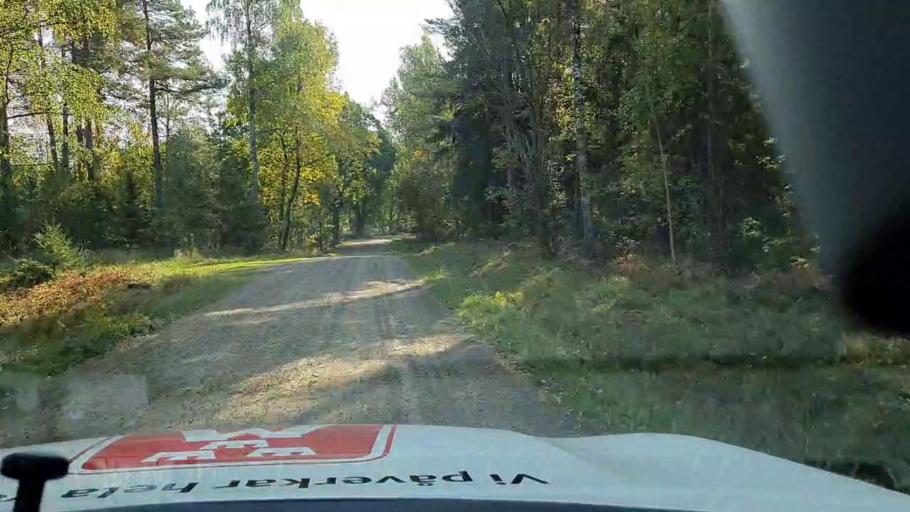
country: SE
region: Soedermanland
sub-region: Eskilstuna Kommun
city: Kvicksund
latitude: 59.3273
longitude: 16.2336
